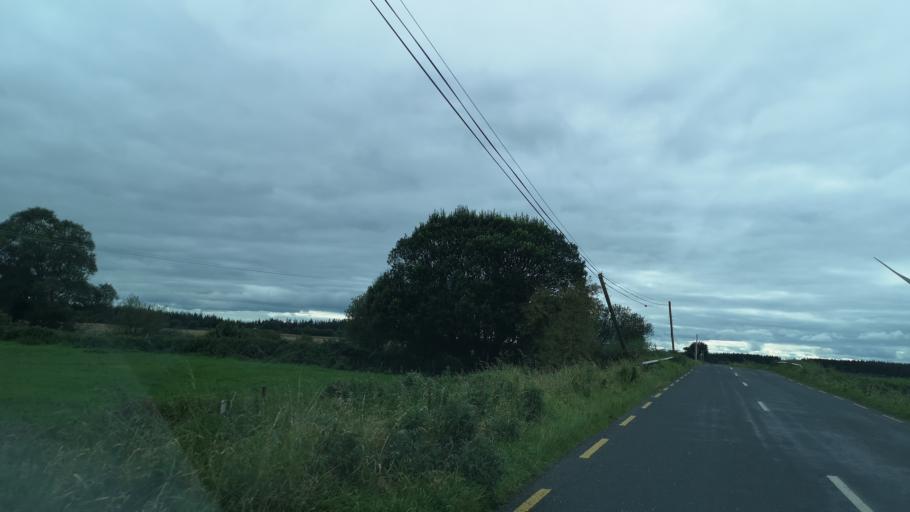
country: IE
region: Leinster
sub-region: Uibh Fhaili
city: Ferbane
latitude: 53.2324
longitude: -7.7582
